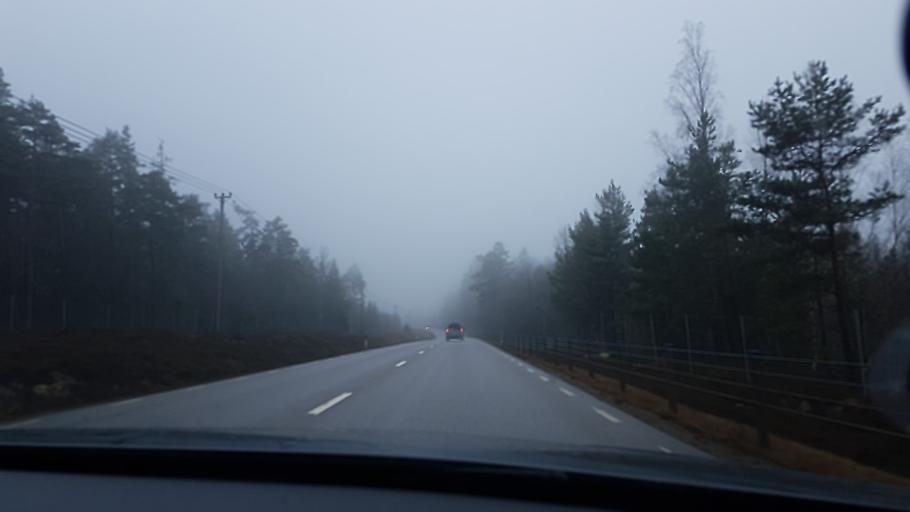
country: SE
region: Vaestra Goetaland
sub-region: Gullspangs Kommun
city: Gullspang
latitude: 58.9381
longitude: 14.0401
